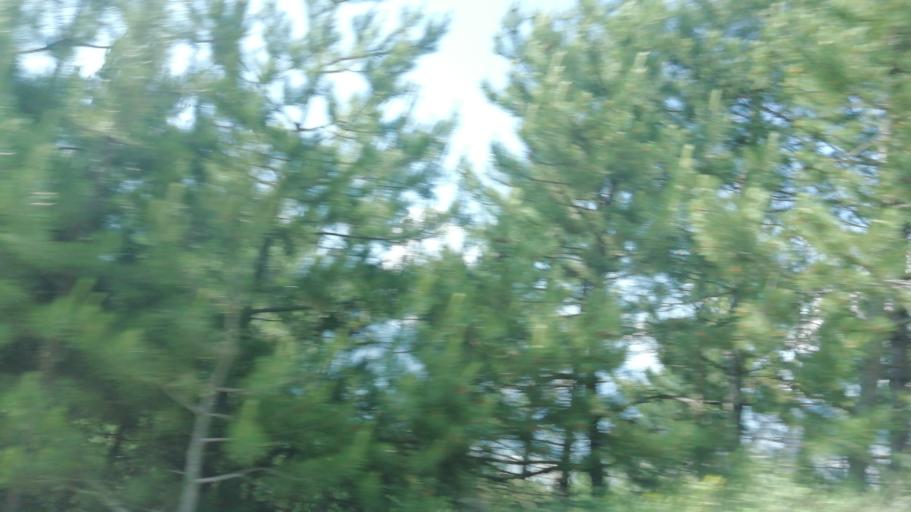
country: TR
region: Karabuk
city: Karabuk
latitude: 41.1246
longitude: 32.5838
